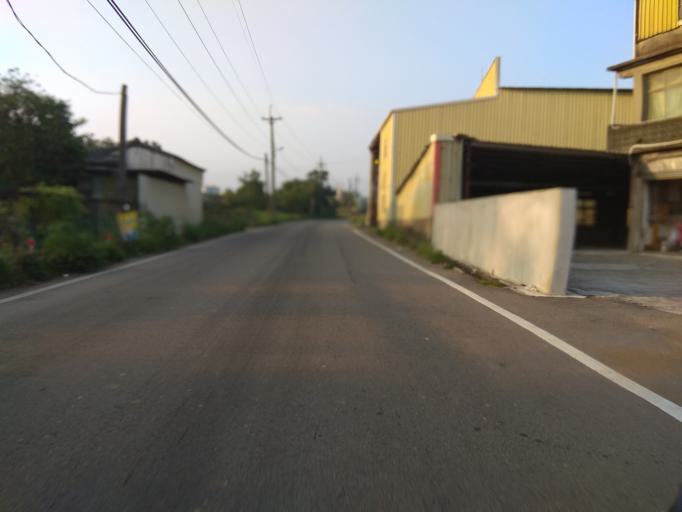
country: TW
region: Taiwan
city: Daxi
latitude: 24.9340
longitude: 121.2095
